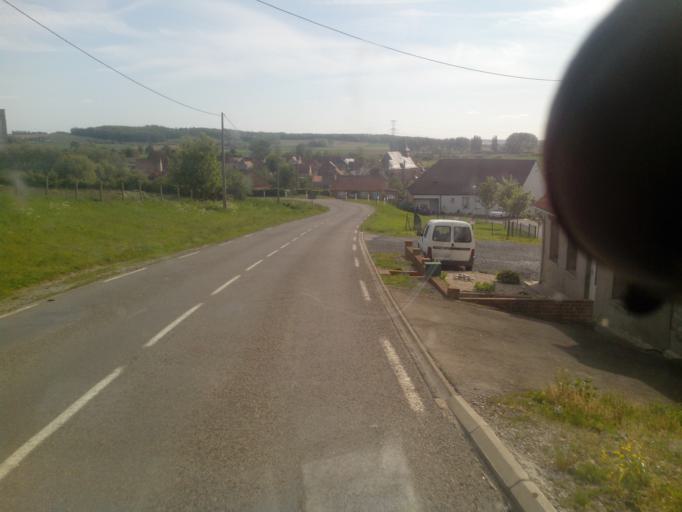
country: FR
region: Nord-Pas-de-Calais
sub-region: Departement du Nord
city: Renescure
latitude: 50.7357
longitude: 2.4121
